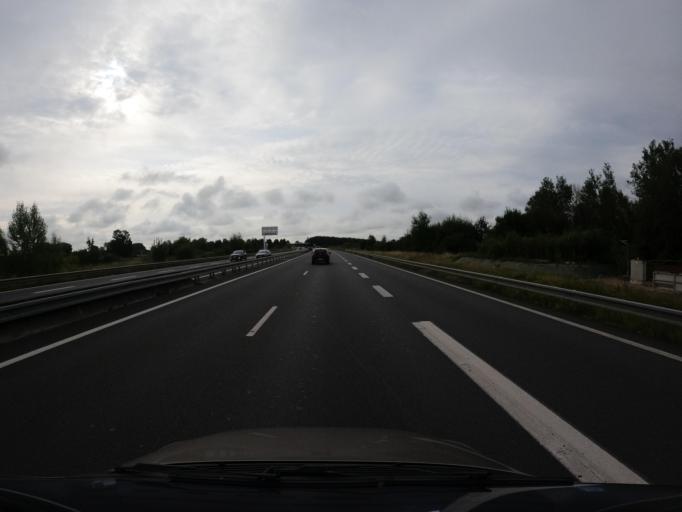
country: FR
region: Centre
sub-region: Departement d'Indre-et-Loire
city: Villandry
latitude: 47.3094
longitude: 0.5124
